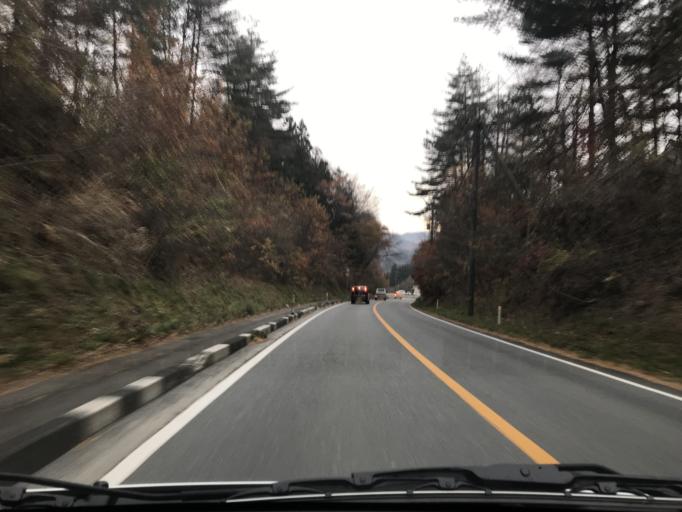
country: JP
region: Iwate
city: Ichinoseki
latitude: 39.0024
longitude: 141.3249
